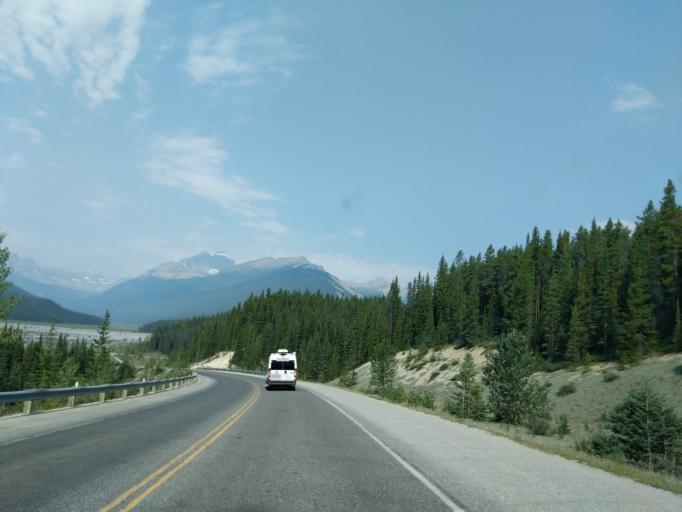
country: CA
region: British Columbia
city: Golden
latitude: 52.0679
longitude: -116.9021
